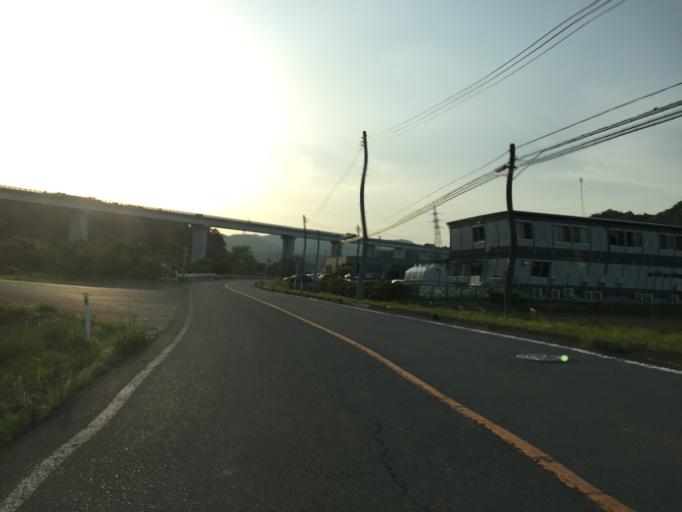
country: JP
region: Fukushima
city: Iwaki
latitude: 37.2144
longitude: 140.9819
